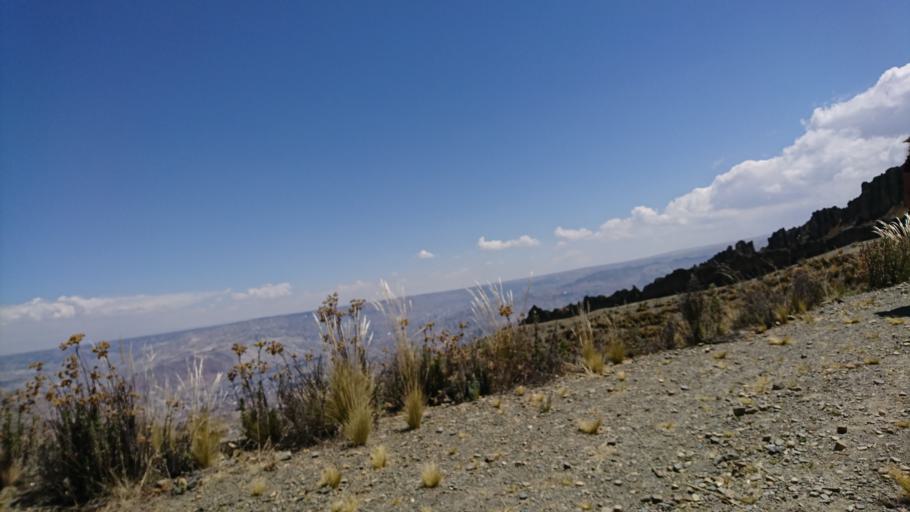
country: BO
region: La Paz
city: La Paz
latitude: -16.5411
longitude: -68.0113
